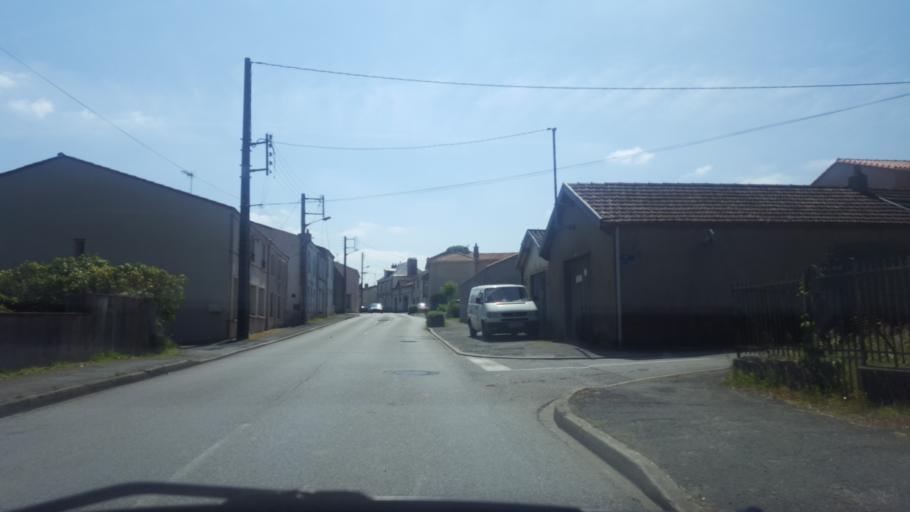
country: FR
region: Pays de la Loire
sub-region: Departement de la Loire-Atlantique
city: La Limouziniere
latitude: 47.0158
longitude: -1.5689
